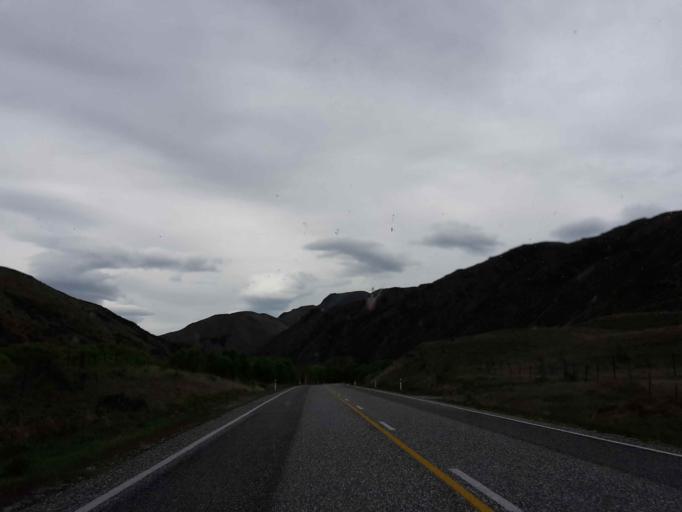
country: NZ
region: Otago
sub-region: Queenstown-Lakes District
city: Wanaka
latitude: -44.6336
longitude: 169.5139
